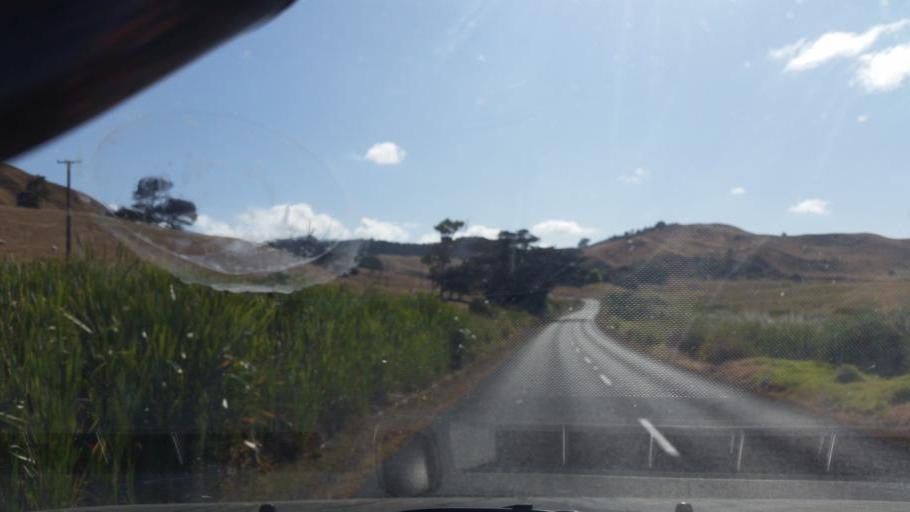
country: NZ
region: Northland
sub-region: Kaipara District
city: Dargaville
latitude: -35.8263
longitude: 173.6747
